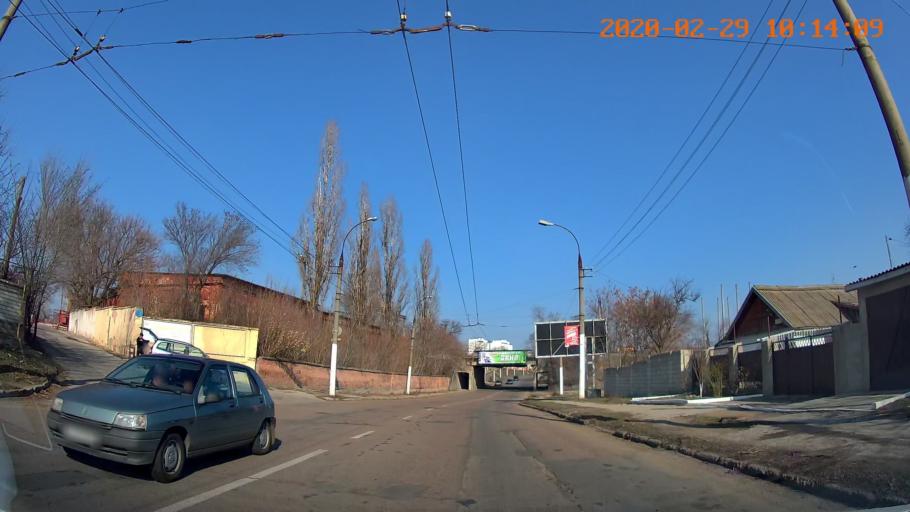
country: MD
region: Telenesti
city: Tiraspolul Nou
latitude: 46.8443
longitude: 29.6443
